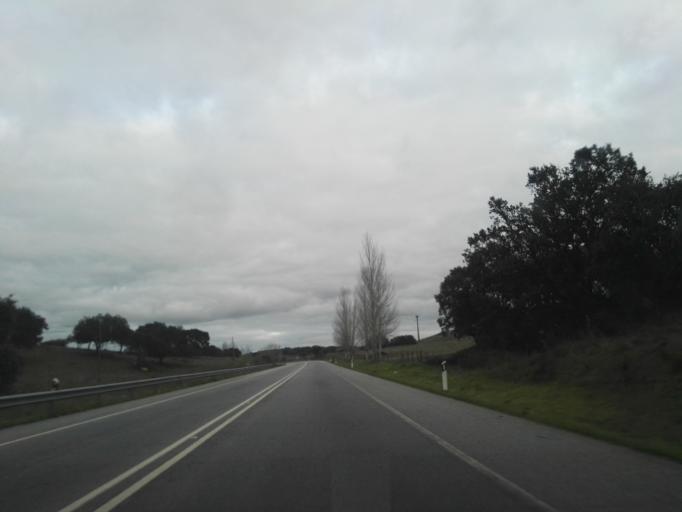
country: PT
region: Evora
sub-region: Montemor-O-Novo
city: Montemor-o-Novo
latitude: 38.6443
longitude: -8.1833
